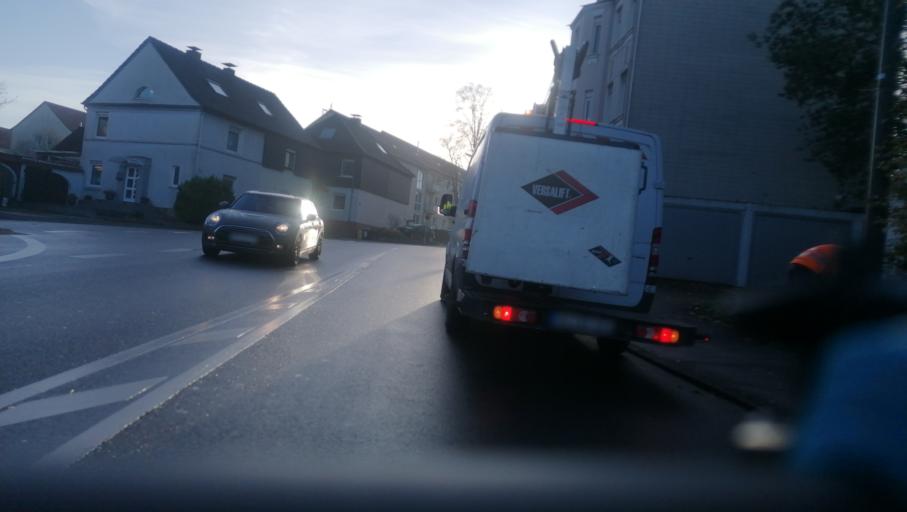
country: DE
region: North Rhine-Westphalia
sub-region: Regierungsbezirk Arnsberg
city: Dortmund
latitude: 51.4738
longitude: 7.4884
